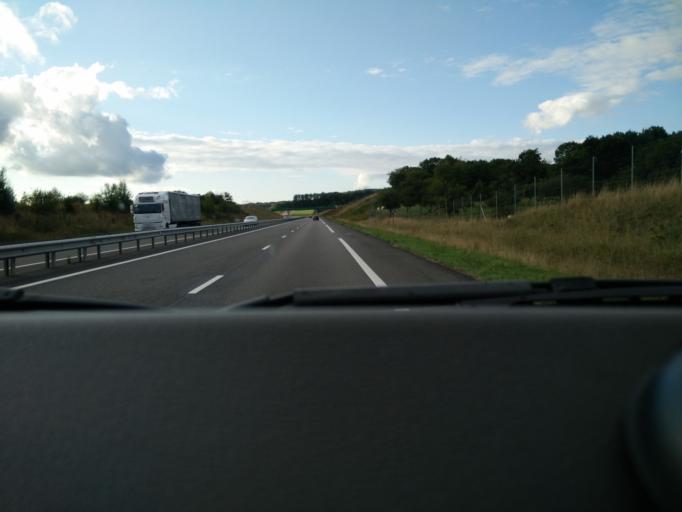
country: FR
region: Lorraine
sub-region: Departement de Meurthe-et-Moselle
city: Baccarat
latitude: 48.4907
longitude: 6.7060
